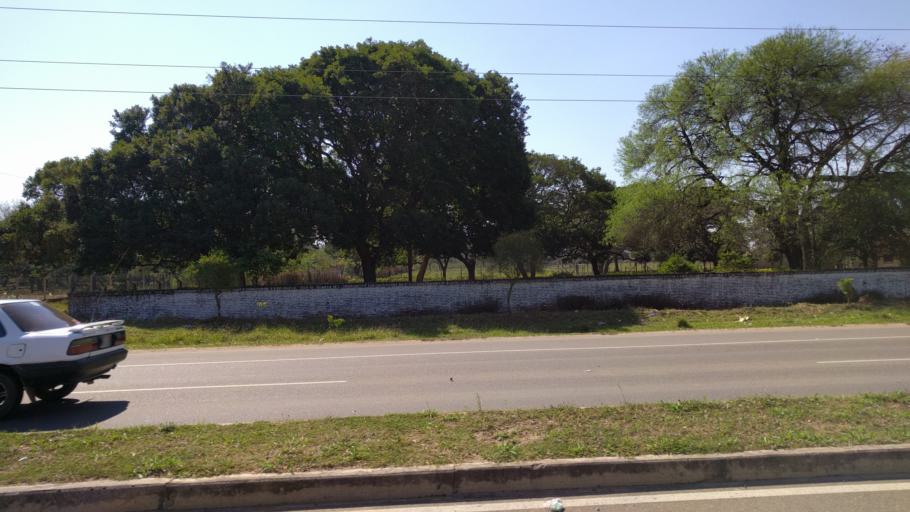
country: BO
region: Santa Cruz
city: Cotoca
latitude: -17.7578
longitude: -63.0078
